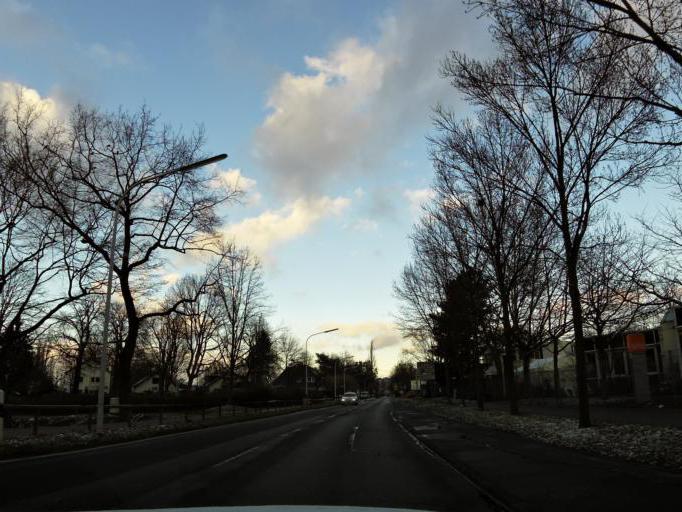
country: DE
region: Hesse
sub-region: Regierungsbezirk Darmstadt
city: Darmstadt
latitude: 49.8895
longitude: 8.6713
